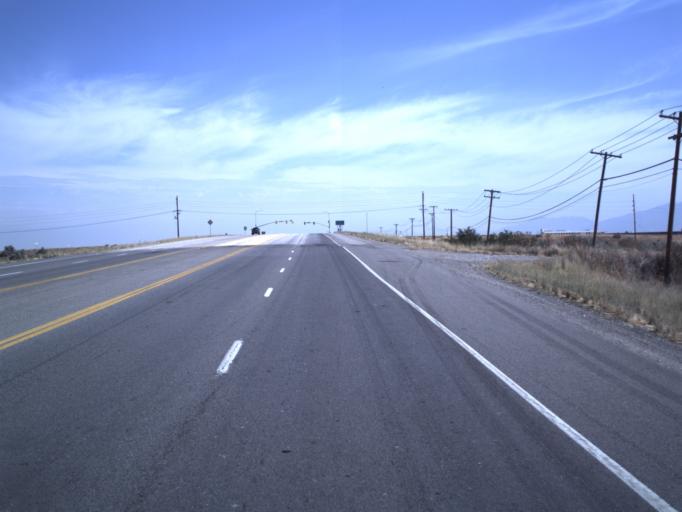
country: US
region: Utah
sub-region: Salt Lake County
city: West Valley City
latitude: 40.7653
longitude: -112.0249
